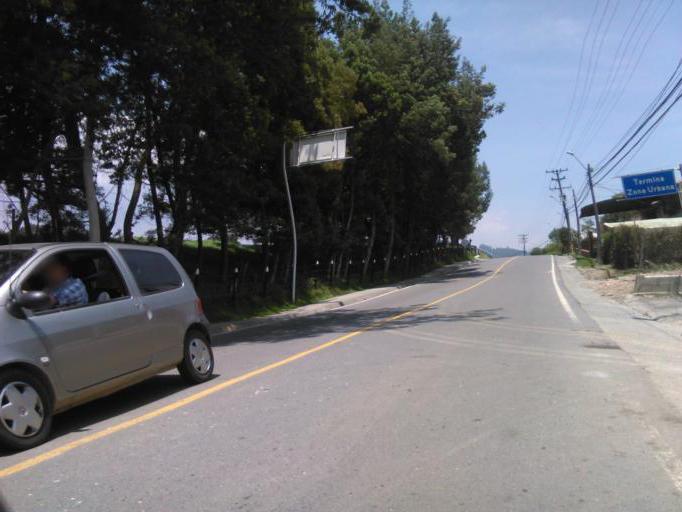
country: CO
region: Antioquia
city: La Union
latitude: 5.9777
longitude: -75.3660
